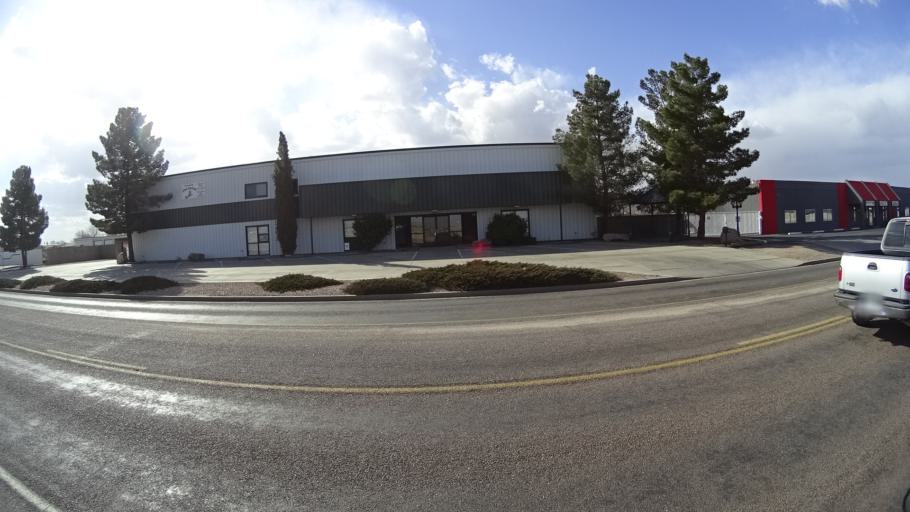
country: US
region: Arizona
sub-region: Mohave County
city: New Kingman-Butler
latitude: 35.2426
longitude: -114.0115
